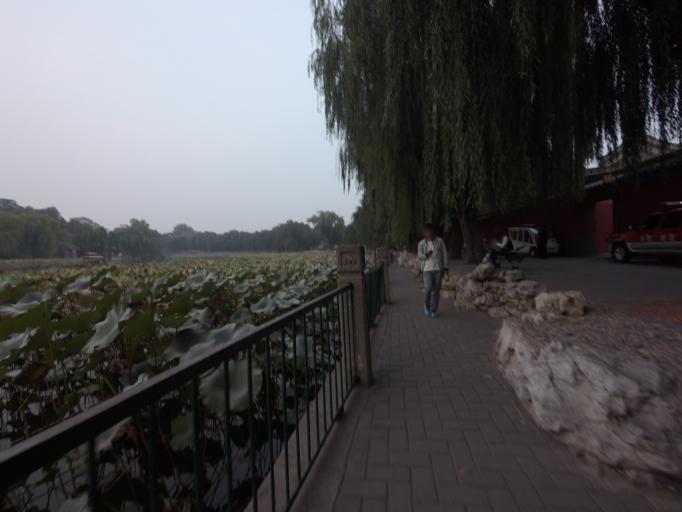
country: CN
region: Beijing
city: Beijing
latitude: 39.9219
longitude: 116.3841
